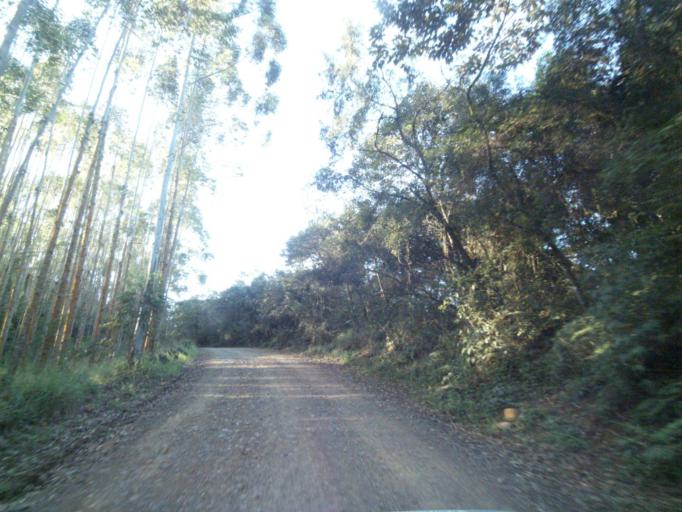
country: BR
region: Parana
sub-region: Telemaco Borba
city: Telemaco Borba
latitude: -24.5045
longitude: -50.5982
